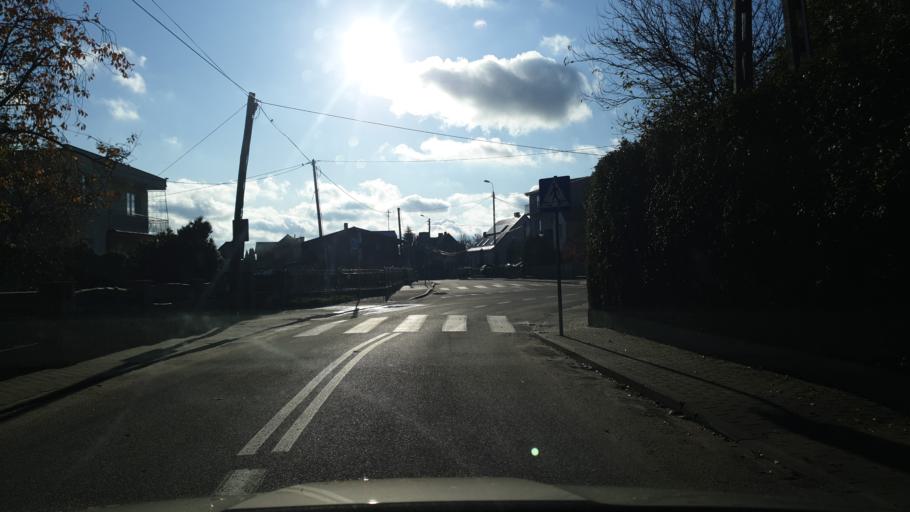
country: PL
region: Pomeranian Voivodeship
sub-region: Powiat pucki
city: Gniezdzewo
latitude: 54.7579
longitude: 18.3992
